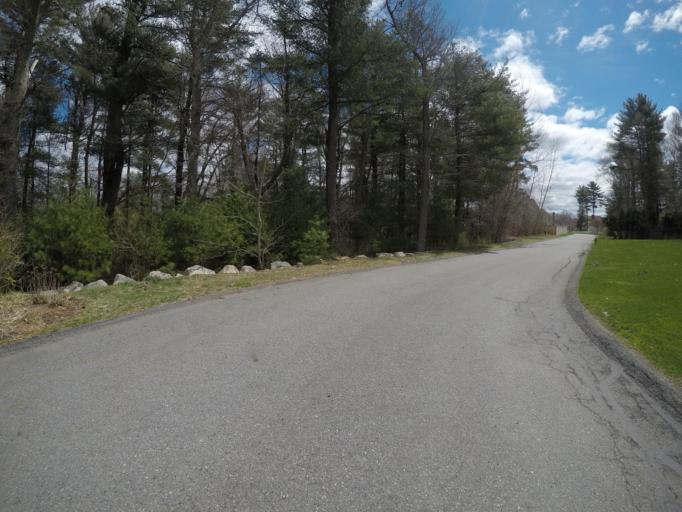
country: US
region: Massachusetts
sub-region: Norfolk County
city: Stoughton
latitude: 42.0803
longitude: -71.0831
